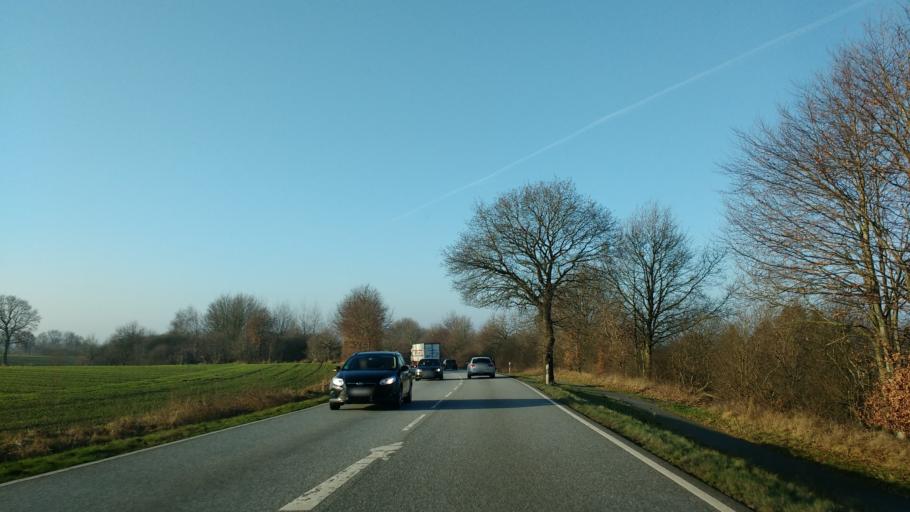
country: DE
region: Schleswig-Holstein
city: Hadenfeld
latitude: 54.0325
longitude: 9.4695
